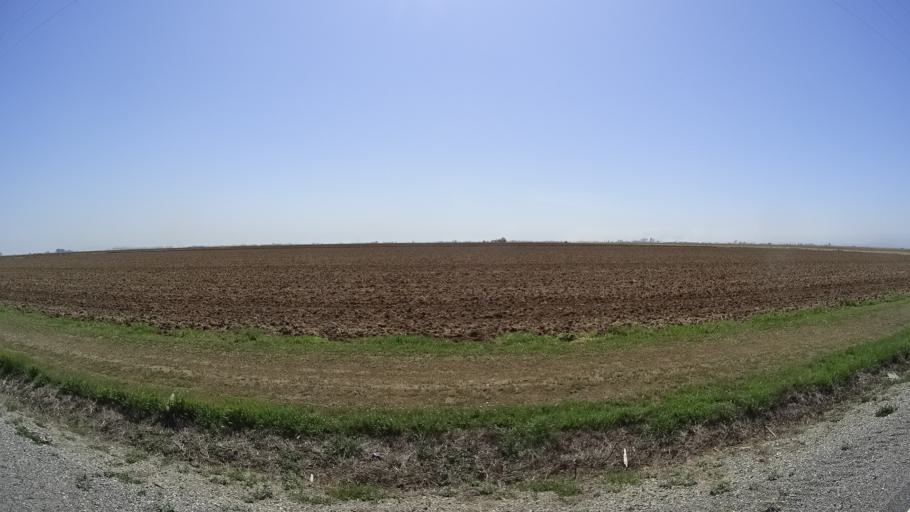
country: US
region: California
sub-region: Glenn County
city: Willows
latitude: 39.4948
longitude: -122.1724
